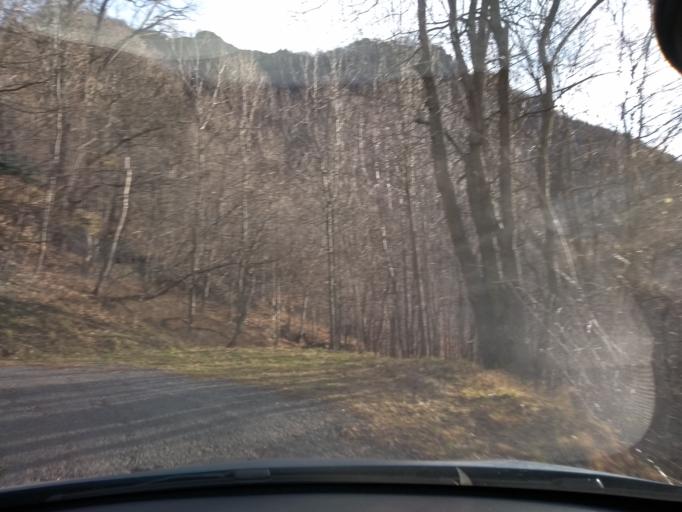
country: IT
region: Piedmont
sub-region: Provincia di Torino
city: Cantoira
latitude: 45.3488
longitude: 7.3838
